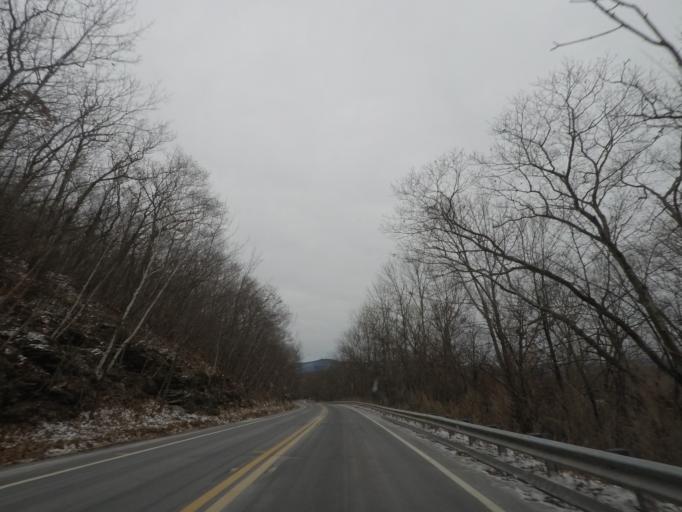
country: US
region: Massachusetts
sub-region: Berkshire County
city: Williamstown
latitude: 42.7132
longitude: -73.2595
